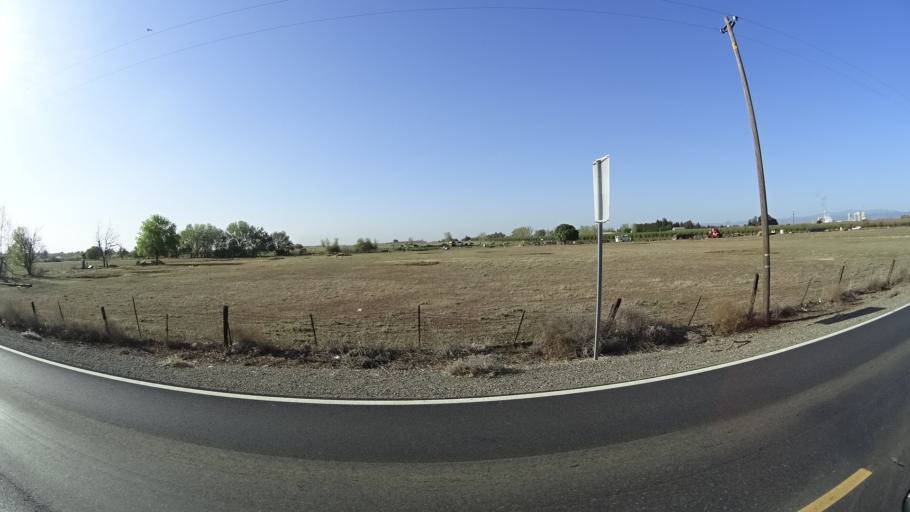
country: US
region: California
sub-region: Glenn County
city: Willows
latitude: 39.5243
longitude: -122.2234
